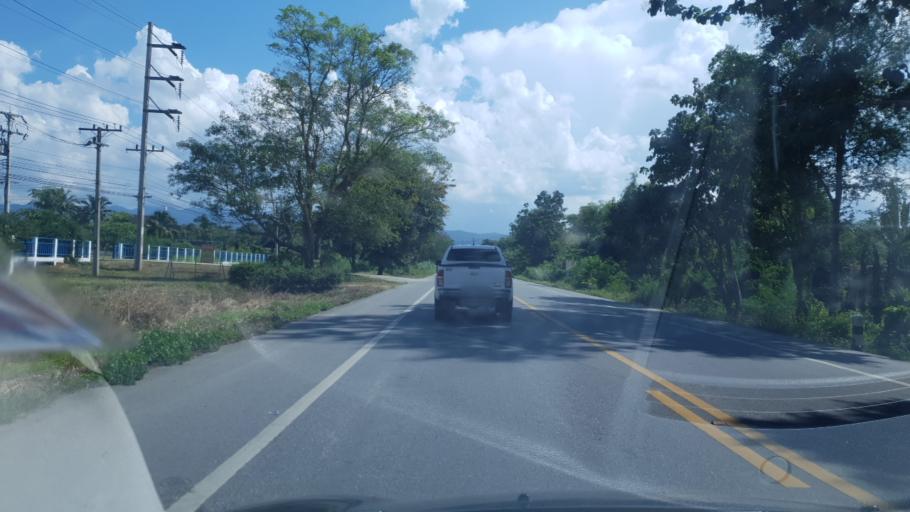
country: TH
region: Chiang Rai
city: Mae Suai
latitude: 19.6292
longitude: 99.5163
